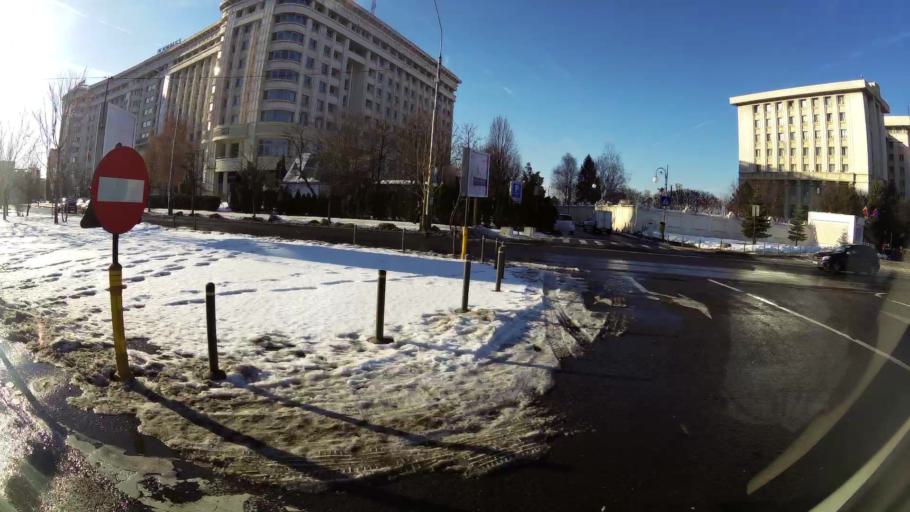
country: RO
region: Bucuresti
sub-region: Municipiul Bucuresti
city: Bucuresti
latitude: 44.4258
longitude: 26.0786
